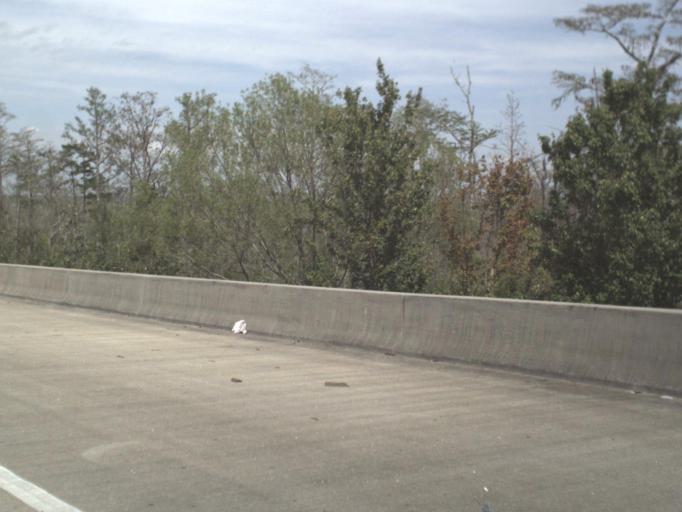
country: US
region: Florida
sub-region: Escambia County
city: Ferry Pass
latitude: 30.5522
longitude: -87.1939
